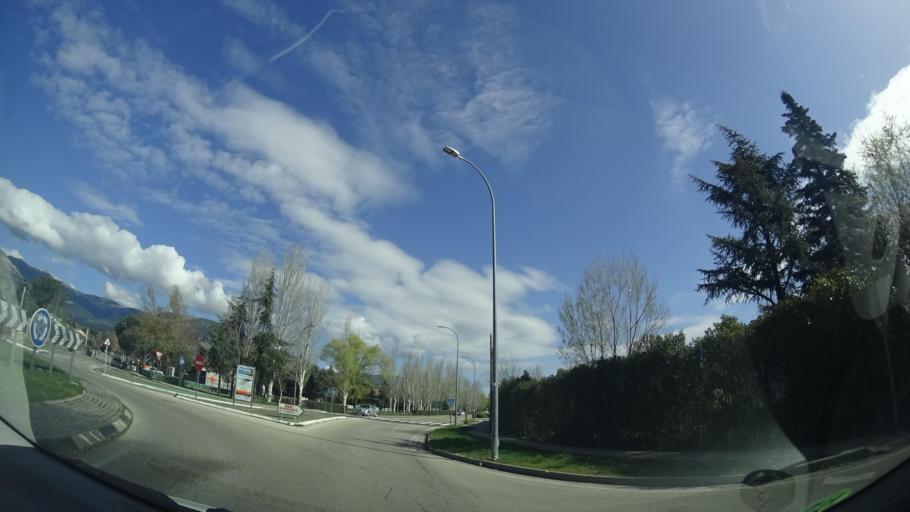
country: ES
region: Madrid
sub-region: Provincia de Madrid
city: Miraflores de la Sierra
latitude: 40.7494
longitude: -3.7828
